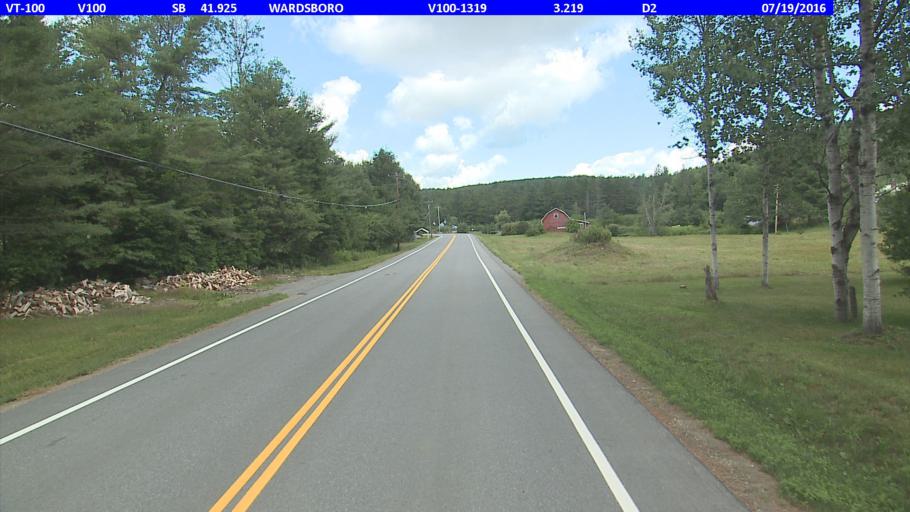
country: US
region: Vermont
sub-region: Windham County
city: Dover
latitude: 43.0441
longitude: -72.8570
